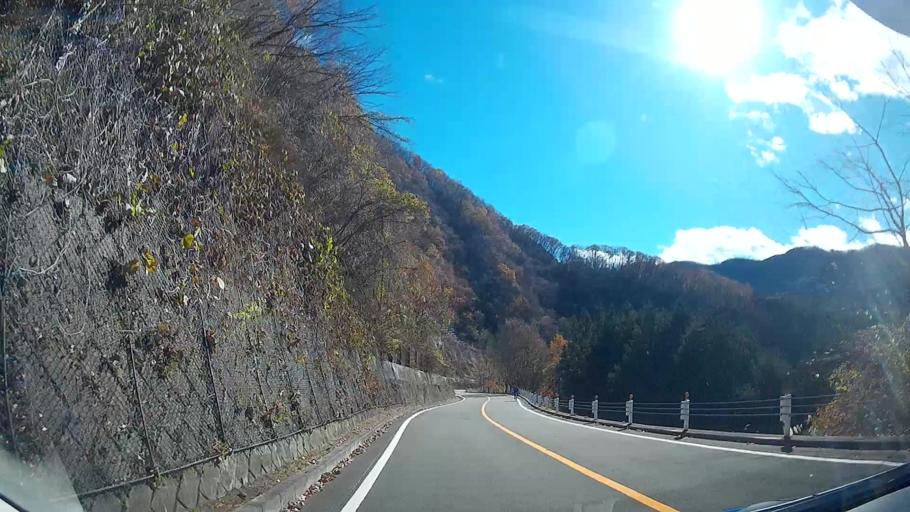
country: JP
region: Yamanashi
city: Uenohara
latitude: 35.7616
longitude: 139.0356
